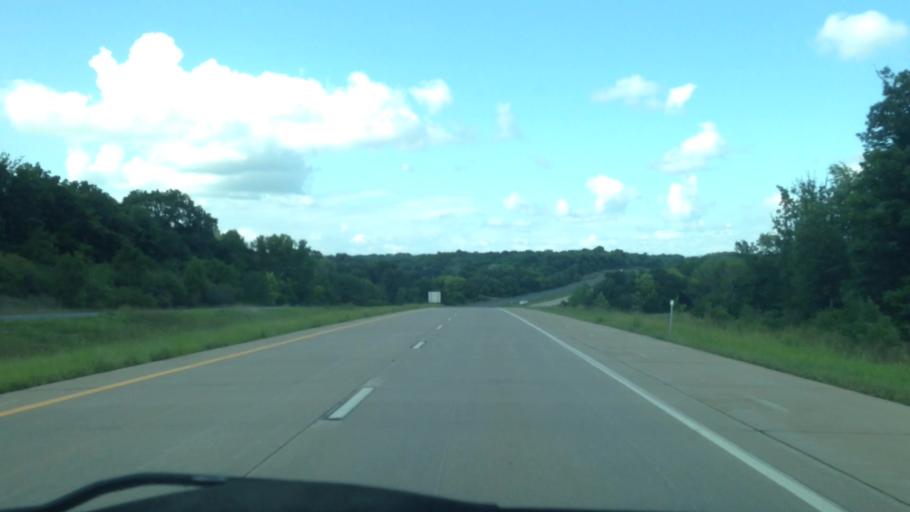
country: US
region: Missouri
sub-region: Lewis County
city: Canton
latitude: 40.1472
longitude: -91.5385
